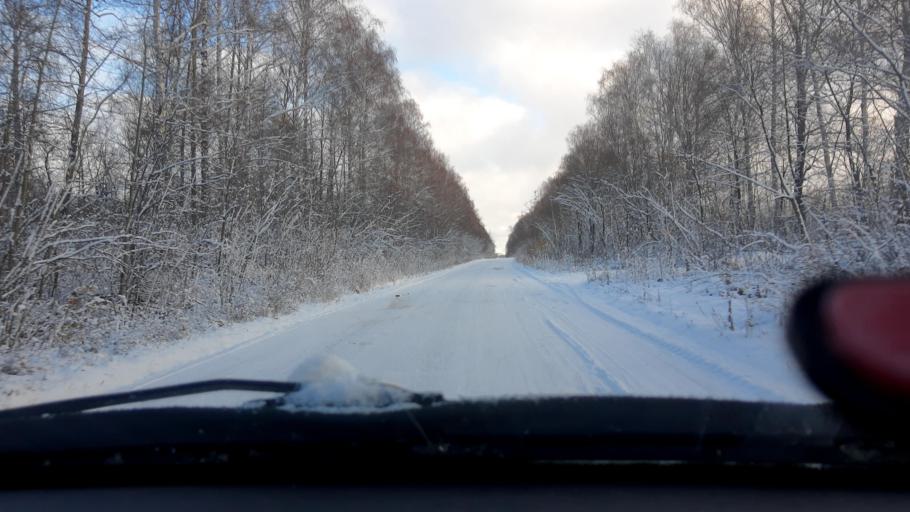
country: RU
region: Bashkortostan
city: Iglino
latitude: 54.8412
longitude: 56.4575
